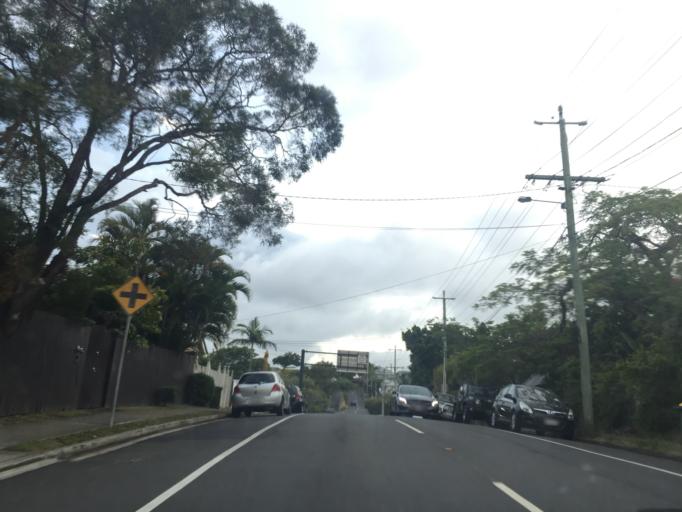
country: AU
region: Queensland
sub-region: Brisbane
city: Milton
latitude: -27.4613
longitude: 152.9970
